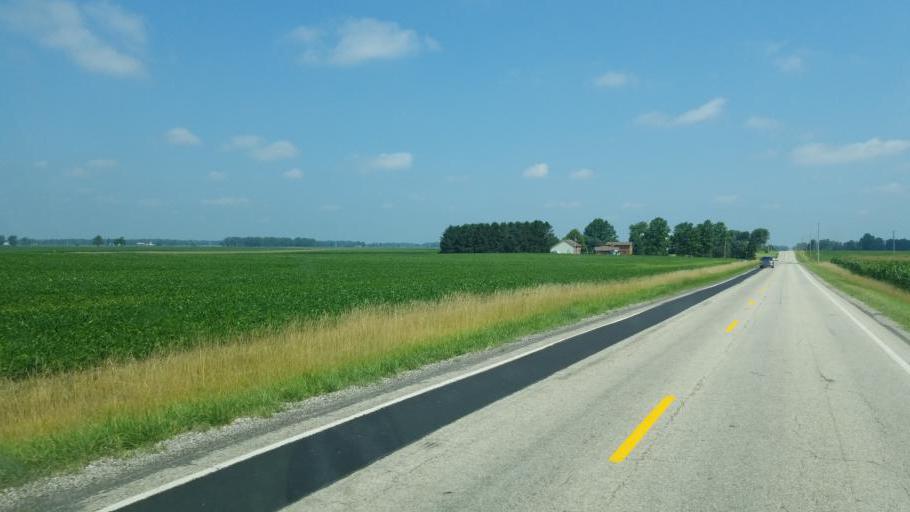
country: US
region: Ohio
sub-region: Crawford County
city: Bucyrus
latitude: 40.9154
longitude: -82.8544
